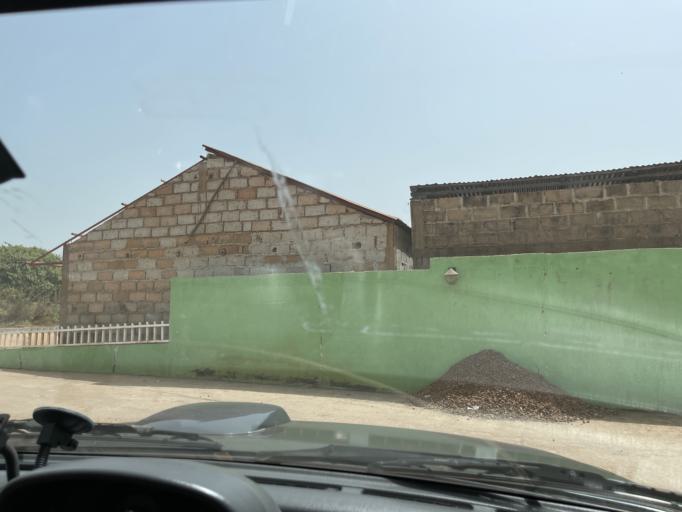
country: SN
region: Ziguinchor
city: Adeane
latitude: 12.3966
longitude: -15.7885
